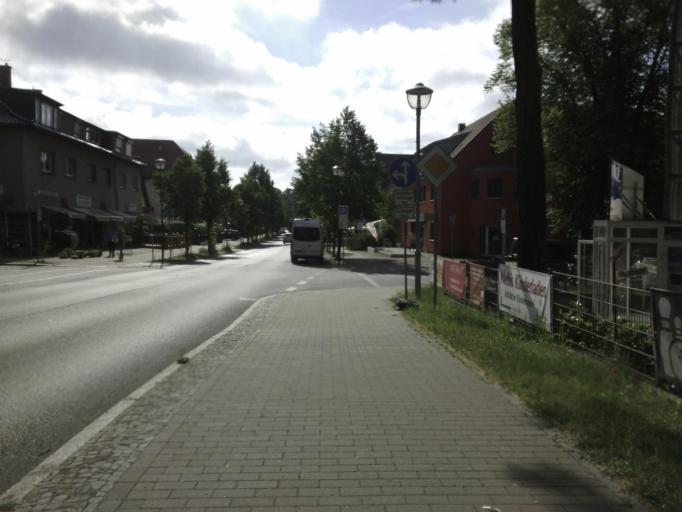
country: DE
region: Brandenburg
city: Hohen Neuendorf
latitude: 52.6693
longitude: 13.2880
